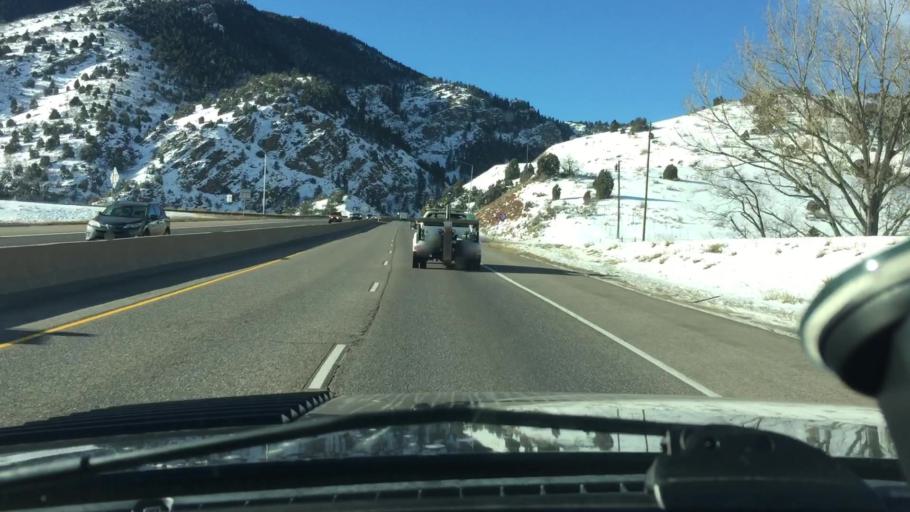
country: US
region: Colorado
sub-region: Jefferson County
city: Indian Hills
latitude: 39.6239
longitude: -105.1931
